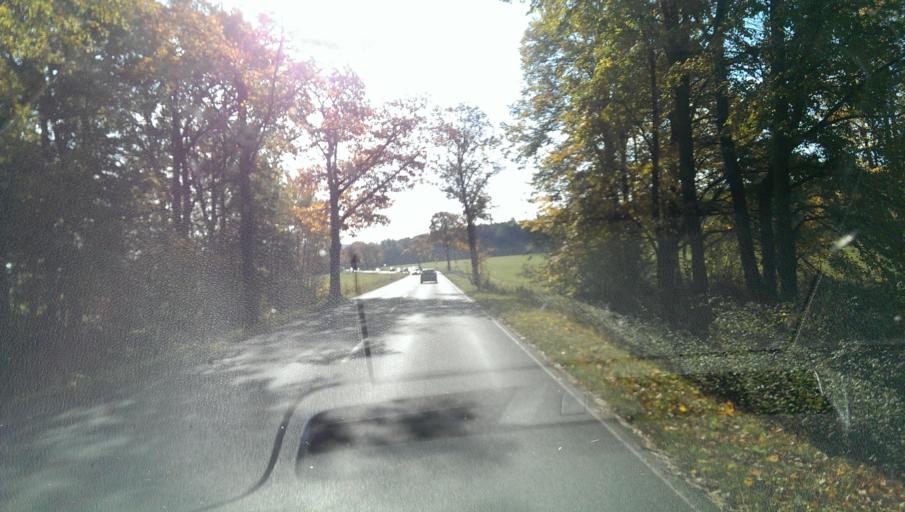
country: DE
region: Saxony
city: Dohma
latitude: 50.8899
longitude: 13.9522
